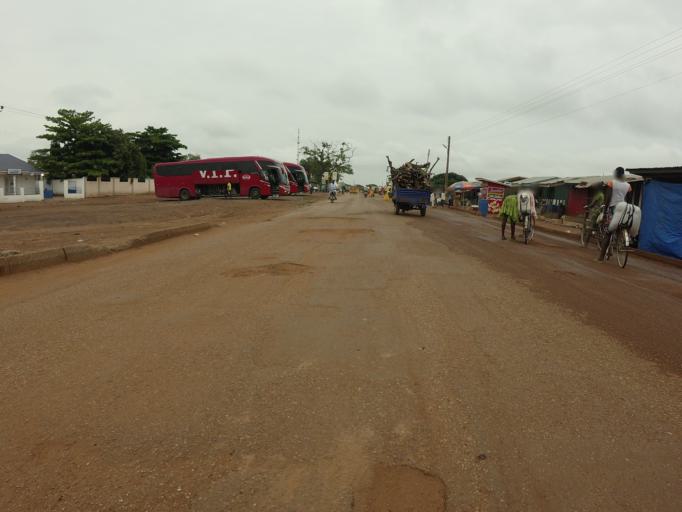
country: GH
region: Northern
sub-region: Yendi
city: Yendi
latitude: 9.4474
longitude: -0.0073
